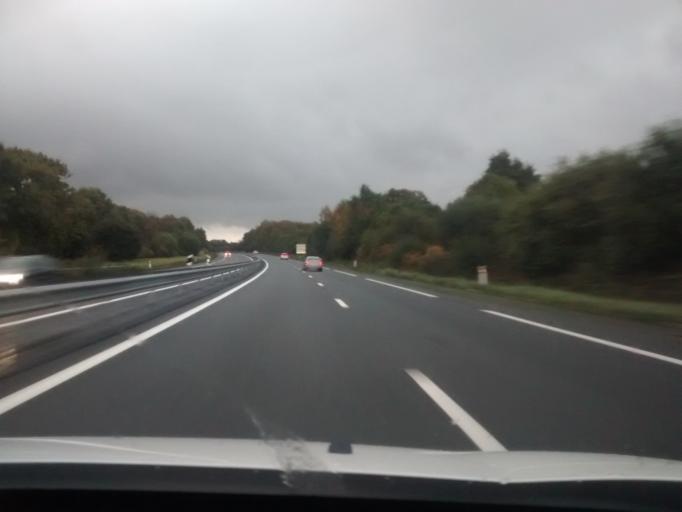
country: FR
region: Brittany
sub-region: Departement d'Ille-et-Vilaine
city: Saint-Pierre-de-Plesguen
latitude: 48.4416
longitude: -1.9248
